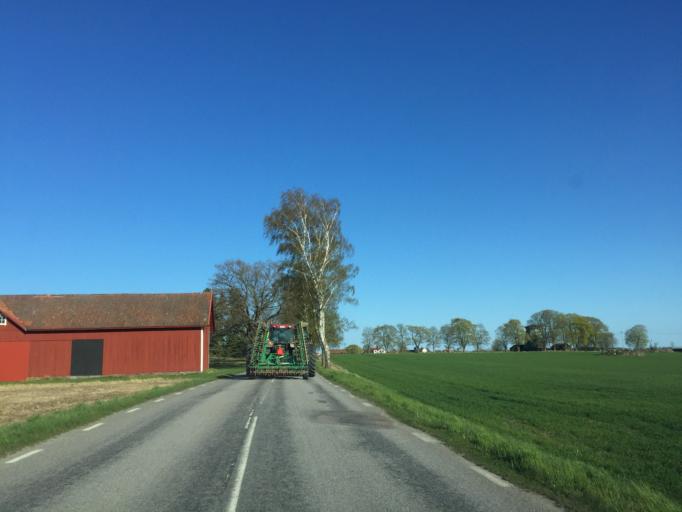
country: SE
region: OErebro
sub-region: Orebro Kommun
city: Odensbacken
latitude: 59.2045
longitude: 15.5436
